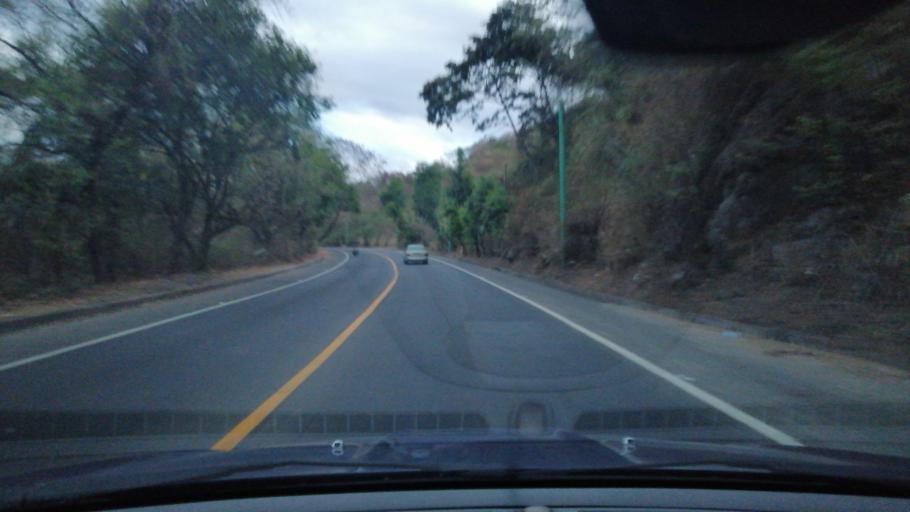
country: SV
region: Santa Ana
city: Santa Ana
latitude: 13.9915
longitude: -89.5418
